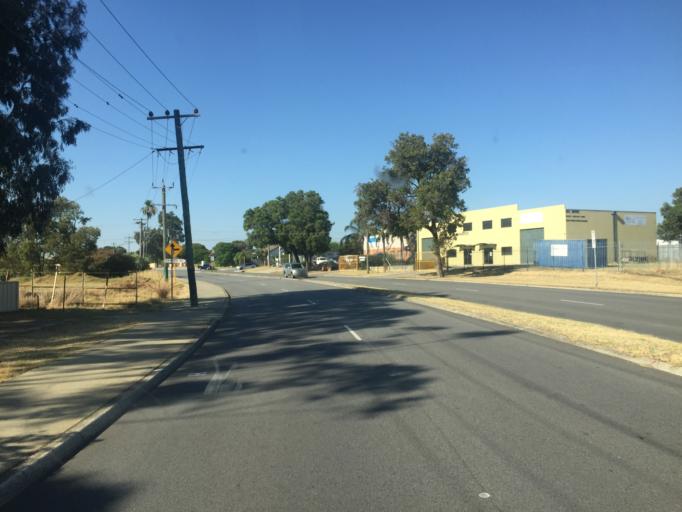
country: AU
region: Western Australia
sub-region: Gosnells
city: Maddington
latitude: -32.0412
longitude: 115.9817
